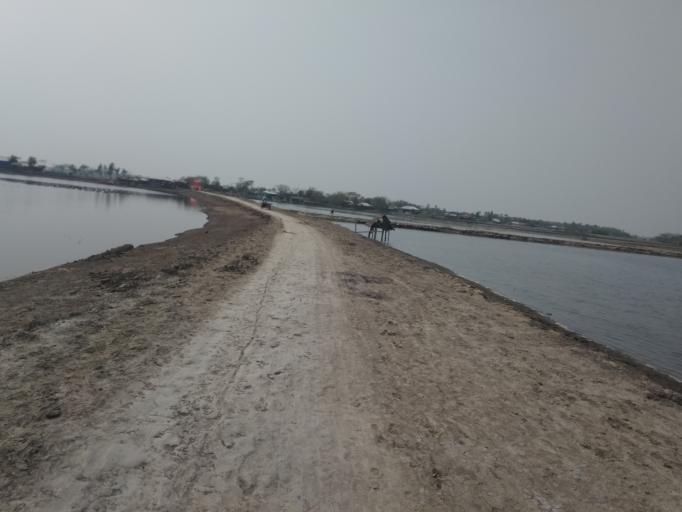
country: IN
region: West Bengal
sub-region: North 24 Parganas
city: Taki
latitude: 22.3473
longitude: 89.2248
